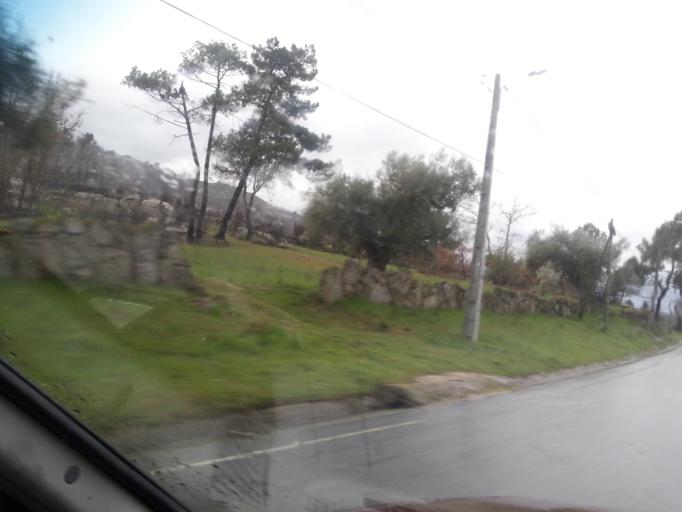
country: PT
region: Guarda
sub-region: Guarda
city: Guarda
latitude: 40.6115
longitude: -7.3034
